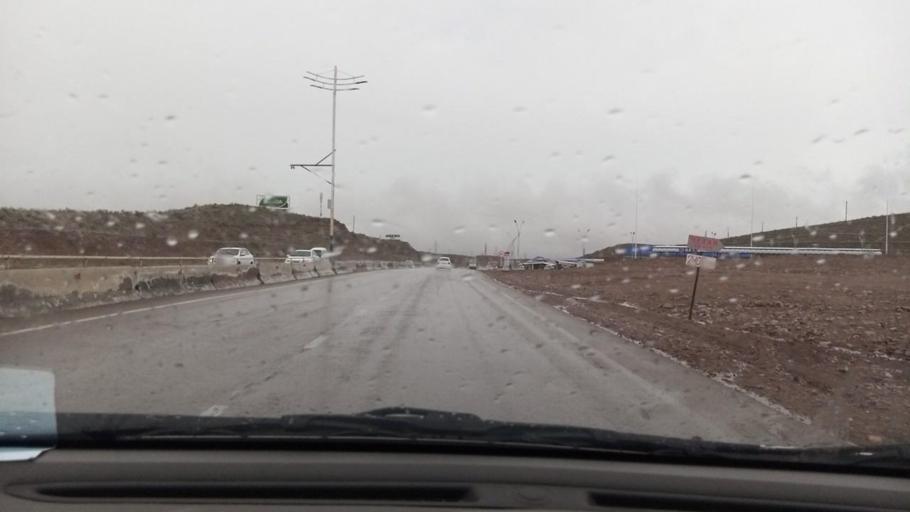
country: UZ
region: Namangan
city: Pop Shahri
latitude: 40.9208
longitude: 70.7385
